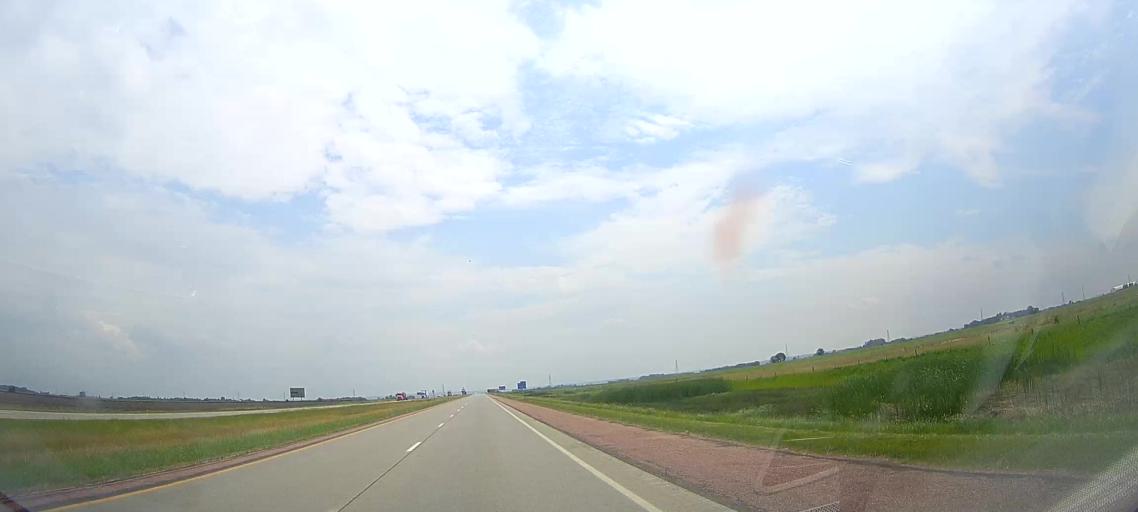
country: US
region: South Dakota
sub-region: Clay County
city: Vermillion
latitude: 42.8005
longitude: -96.7961
